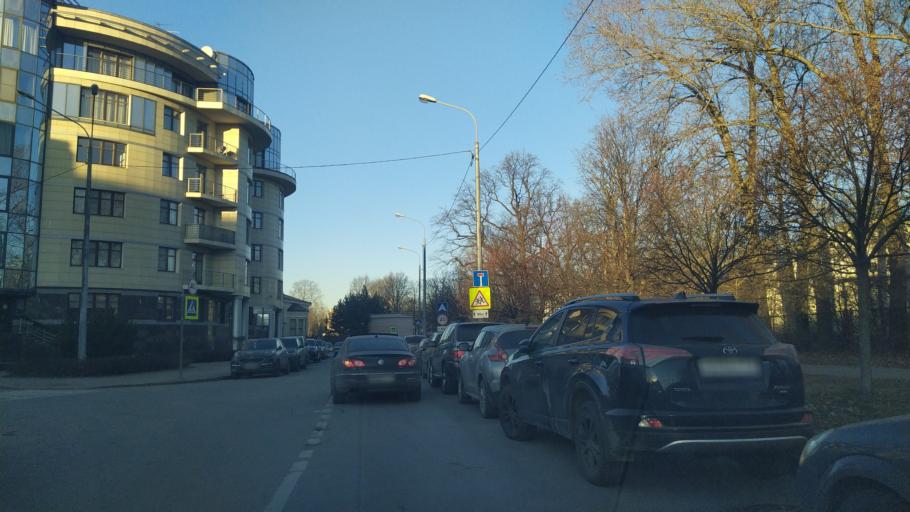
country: RU
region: St.-Petersburg
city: Novaya Derevnya
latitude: 59.9732
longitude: 30.2759
